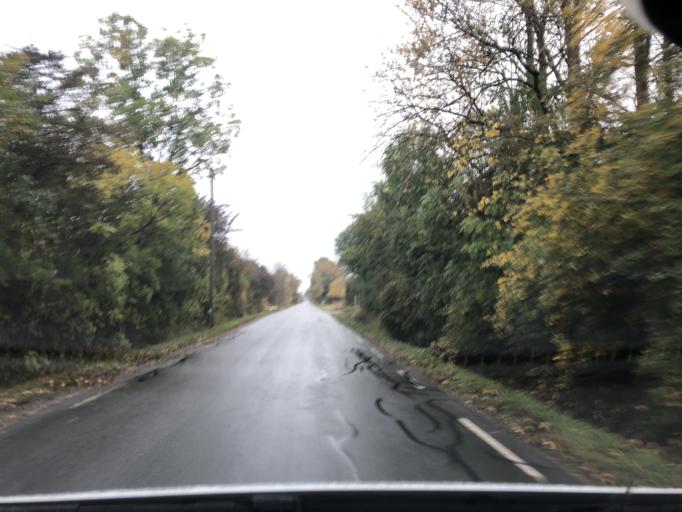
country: DK
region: Capital Region
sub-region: Tarnby Kommune
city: Tarnby
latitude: 55.5729
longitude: 12.6025
